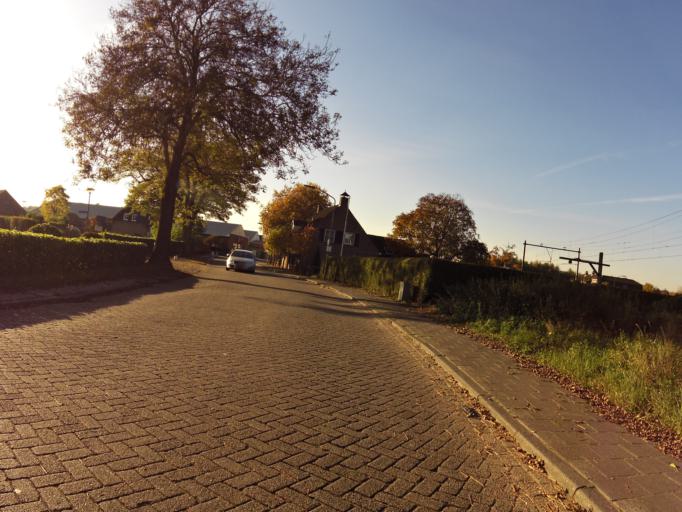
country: NL
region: North Brabant
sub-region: Gemeente Boxtel
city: Boxtel
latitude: 51.5887
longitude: 5.3109
